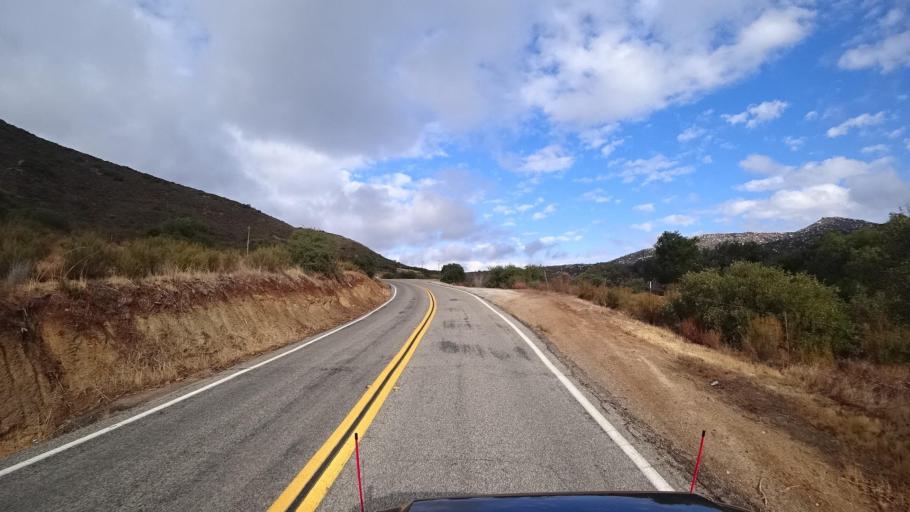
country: MX
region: Baja California
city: Tecate
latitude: 32.6235
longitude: -116.6222
